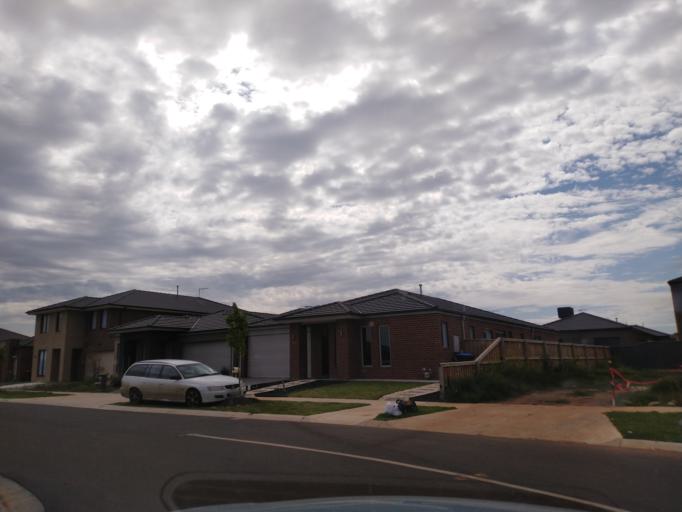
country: AU
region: Victoria
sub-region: Wyndham
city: Williams Landing
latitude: -37.8483
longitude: 144.7169
